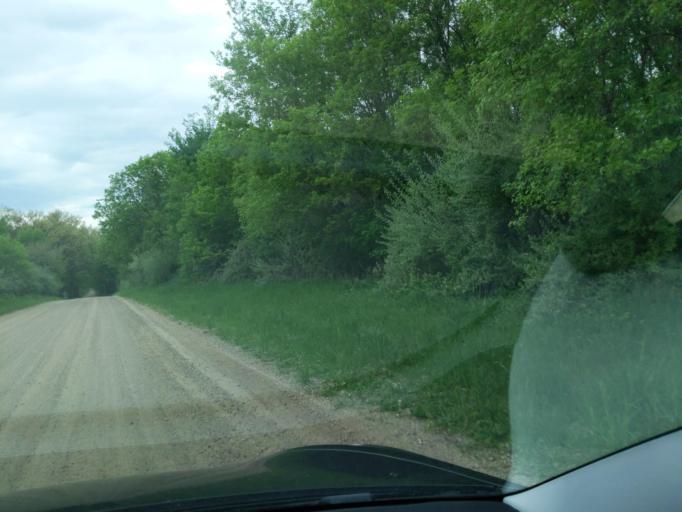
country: US
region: Michigan
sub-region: Ingham County
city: Stockbridge
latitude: 42.5141
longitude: -84.2855
